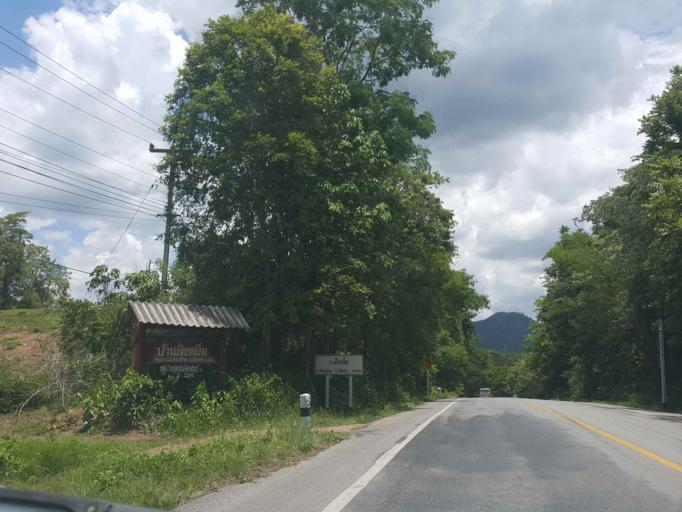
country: TH
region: Nan
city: Wiang Sa
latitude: 18.5241
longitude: 100.5699
